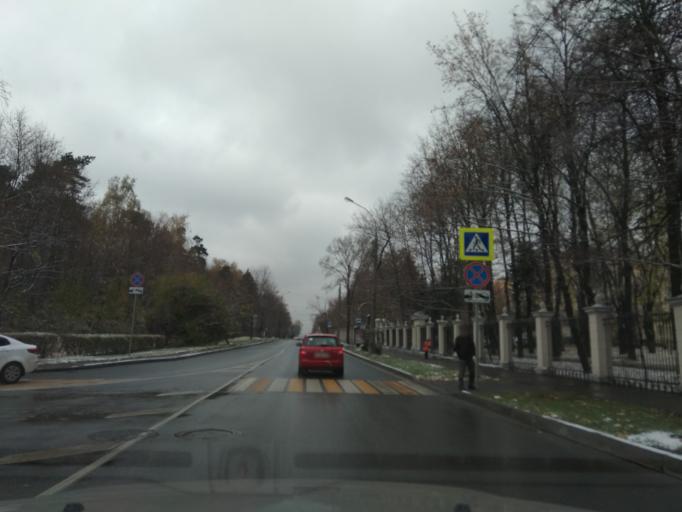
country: RU
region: Moscow
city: Pokrovskoye-Streshnevo
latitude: 55.8028
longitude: 37.4769
